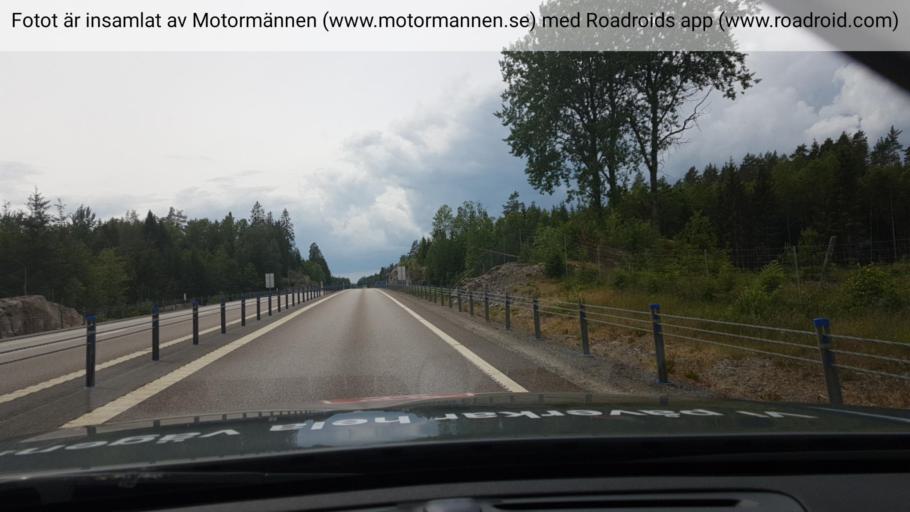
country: SE
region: OErebro
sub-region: Askersunds Kommun
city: Askersund
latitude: 58.8172
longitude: 14.8677
